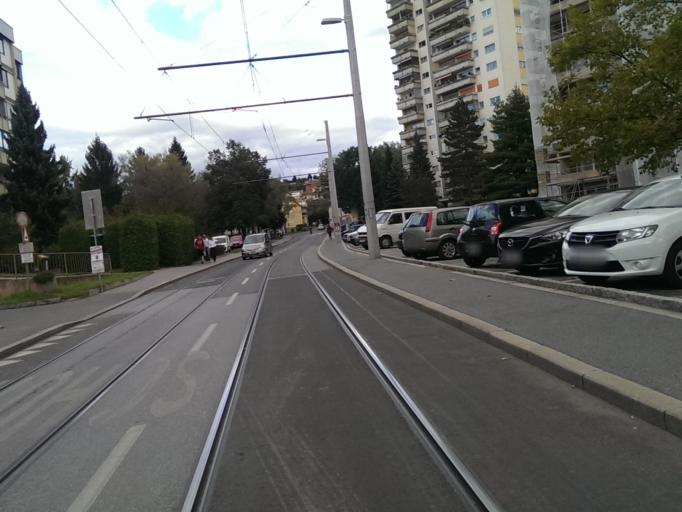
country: AT
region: Styria
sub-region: Graz Stadt
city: Graz
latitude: 47.0609
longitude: 15.4704
